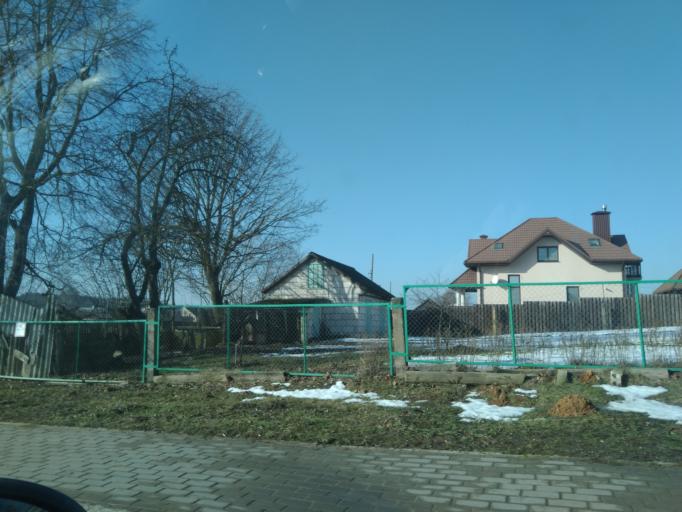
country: BY
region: Minsk
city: Nyasvizh
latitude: 53.2094
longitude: 26.6633
